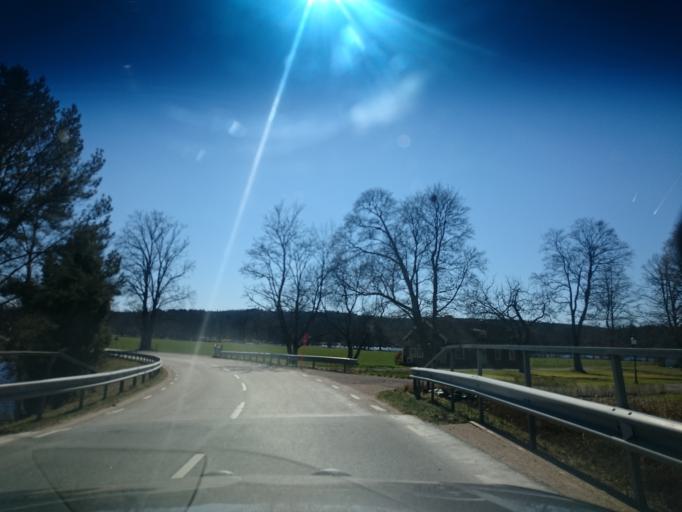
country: SE
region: Kronoberg
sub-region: Vaxjo Kommun
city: Braas
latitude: 57.1968
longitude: 14.9577
